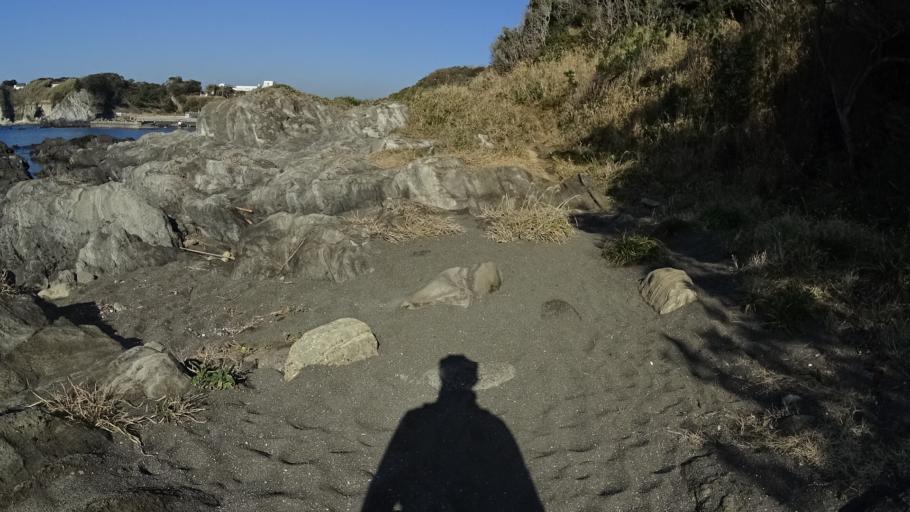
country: JP
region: Kanagawa
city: Miura
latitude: 35.1918
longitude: 139.6087
